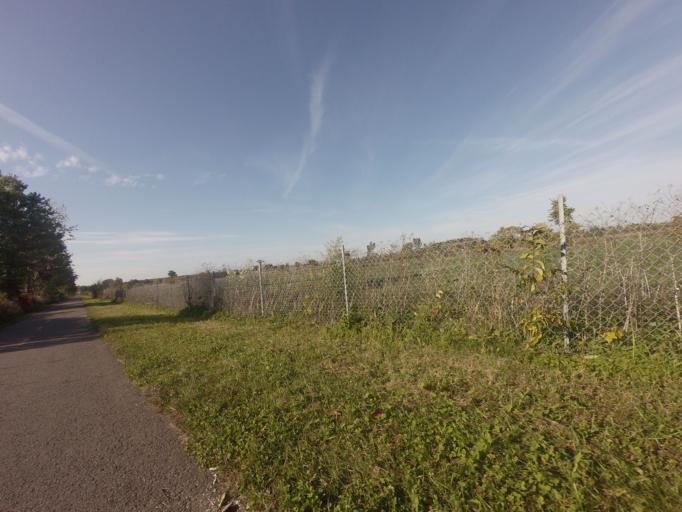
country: CA
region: Quebec
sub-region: Laurentides
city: Blainville
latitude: 45.7185
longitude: -73.9272
